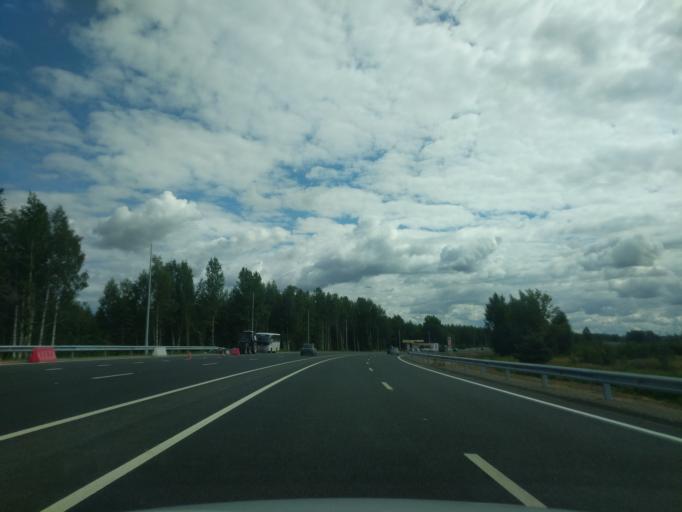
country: RU
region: Kostroma
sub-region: Kostromskoy Rayon
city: Kostroma
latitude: 57.7396
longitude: 40.8629
